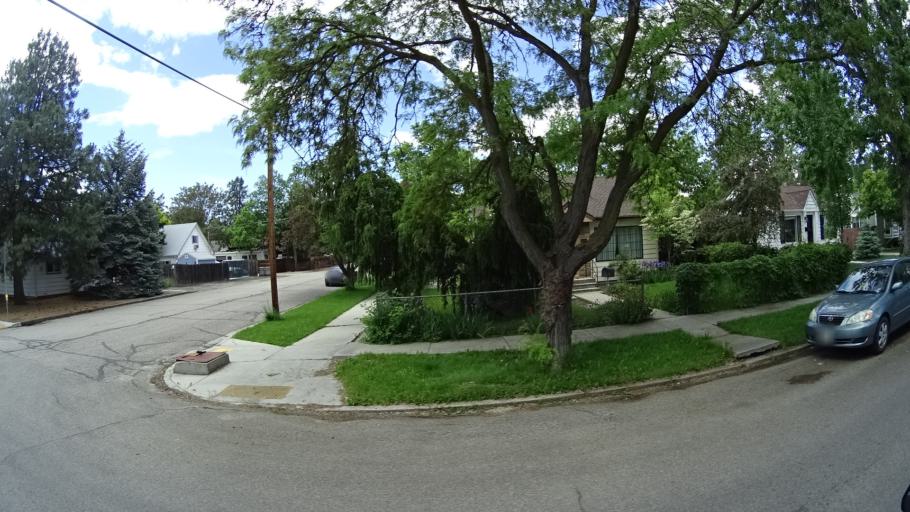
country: US
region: Idaho
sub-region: Ada County
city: Boise
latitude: 43.5921
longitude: -116.1986
